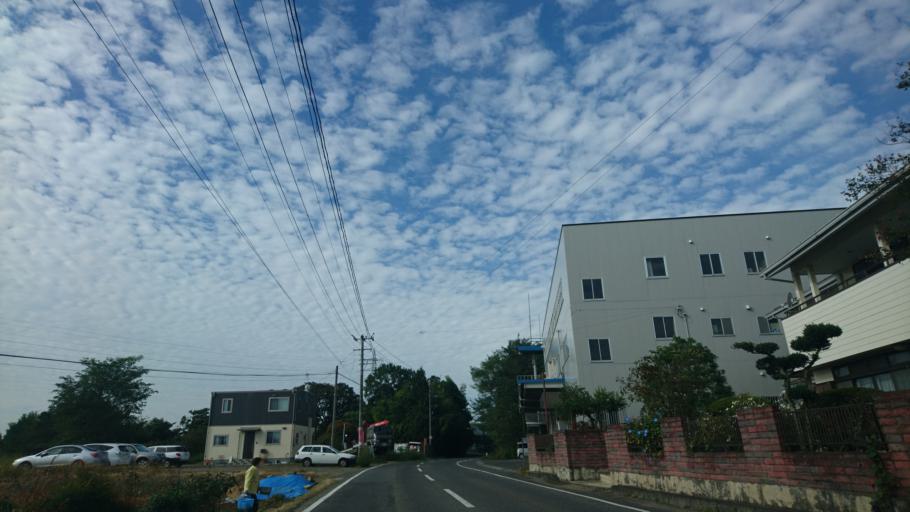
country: JP
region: Fukushima
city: Sukagawa
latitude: 37.3393
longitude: 140.3531
